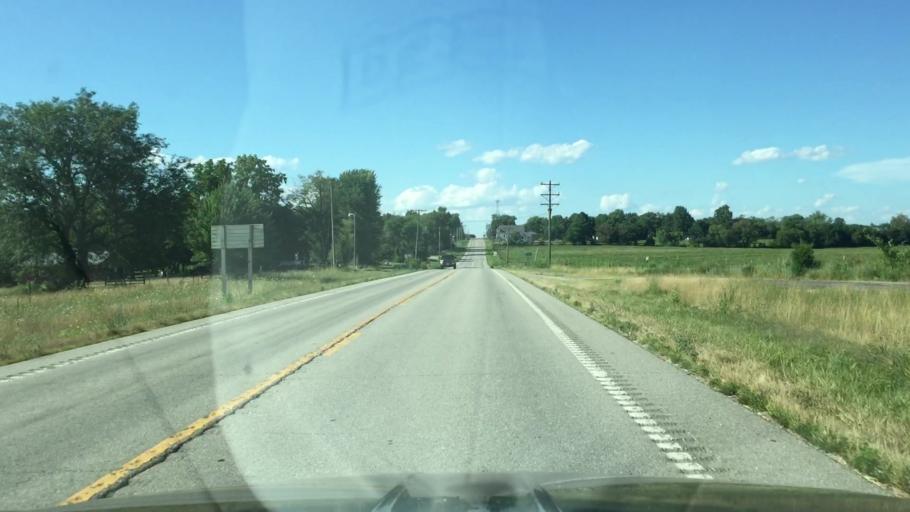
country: US
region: Missouri
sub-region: Moniteau County
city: Tipton
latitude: 38.5614
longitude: -92.7973
